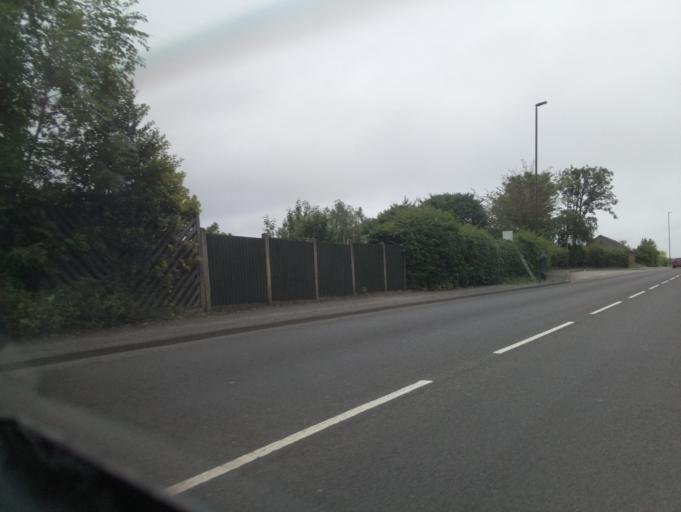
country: GB
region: England
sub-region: Derbyshire
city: Swadlincote
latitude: 52.7661
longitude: -1.5919
